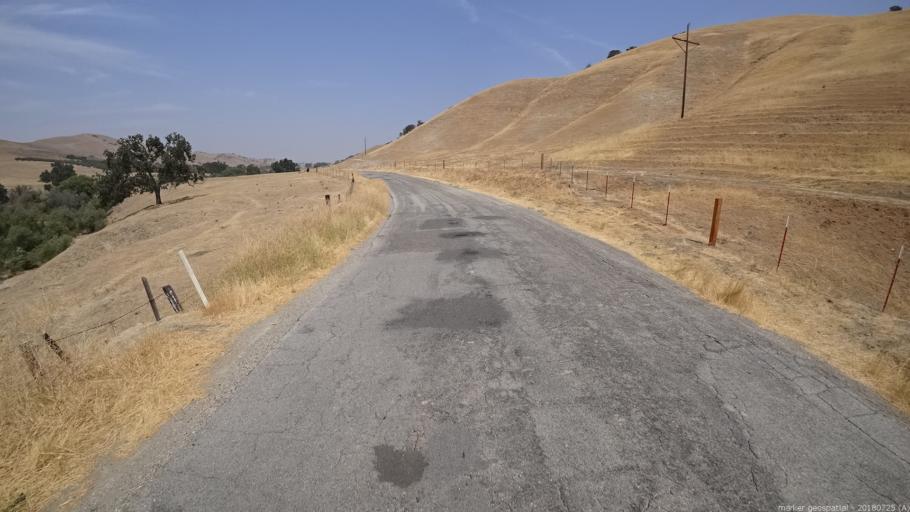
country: US
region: California
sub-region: San Luis Obispo County
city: San Miguel
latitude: 35.7859
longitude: -120.6840
